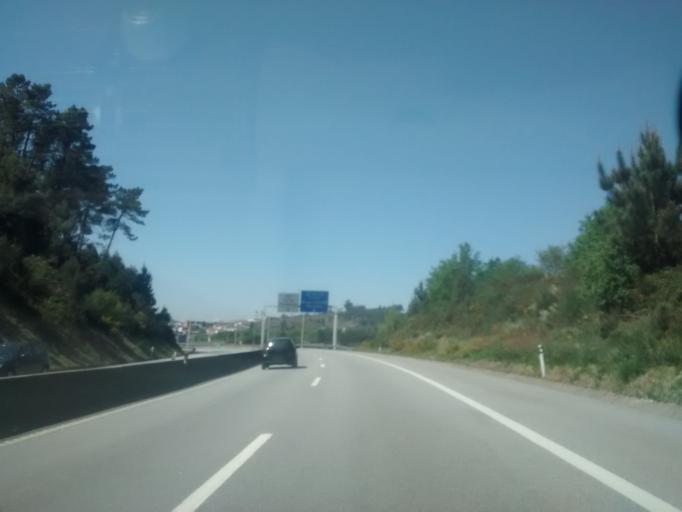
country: PT
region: Braga
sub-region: Braga
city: Braga
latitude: 41.5193
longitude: -8.4381
